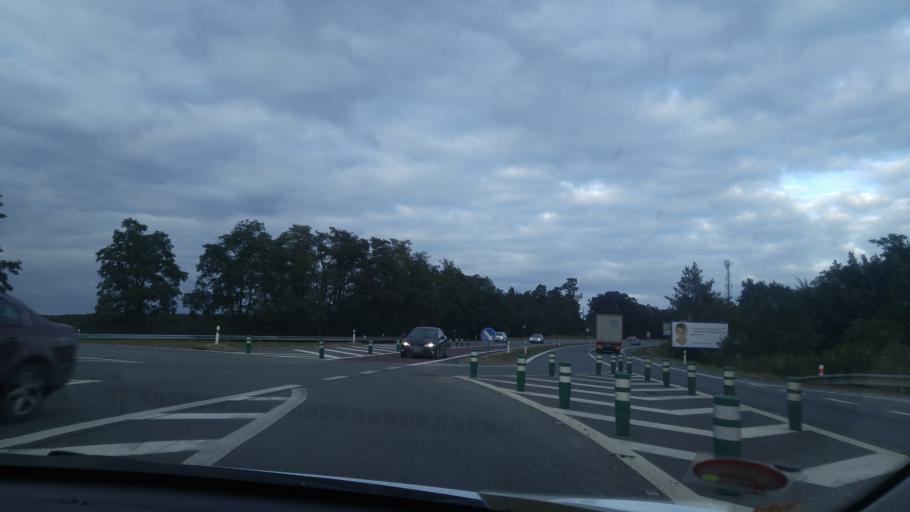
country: CZ
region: South Moravian
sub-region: Okres Brno-Venkov
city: Rosice
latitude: 49.1924
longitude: 16.4252
